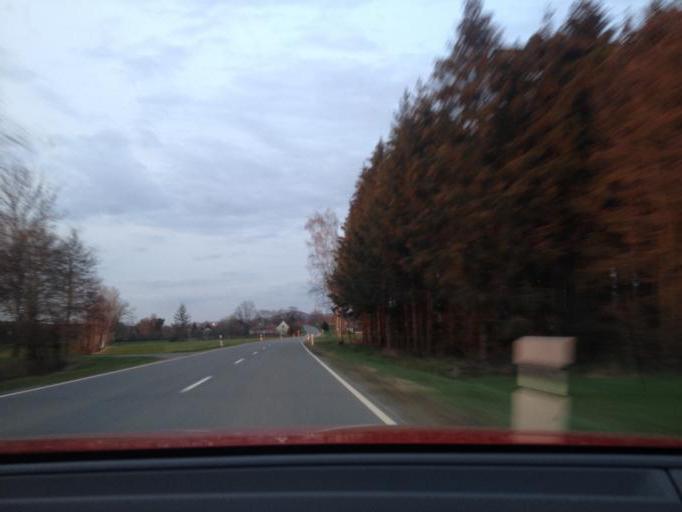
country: DE
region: Bavaria
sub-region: Upper Palatinate
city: Kemnath
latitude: 49.8412
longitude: 11.8510
